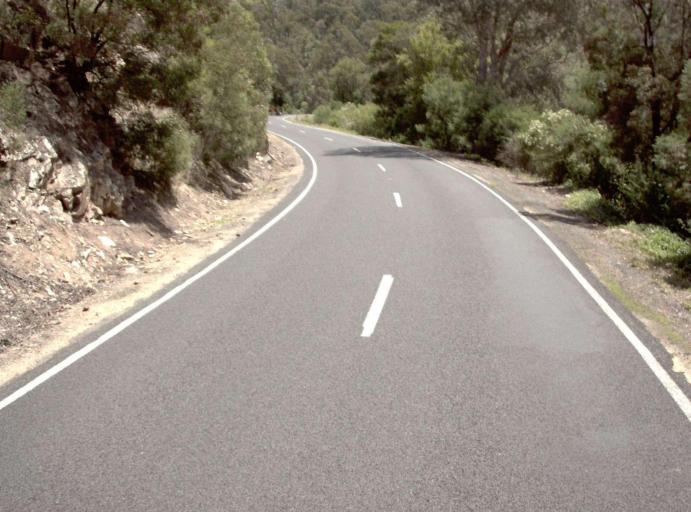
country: AU
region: Victoria
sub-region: East Gippsland
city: Lakes Entrance
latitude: -37.5514
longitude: 147.8762
